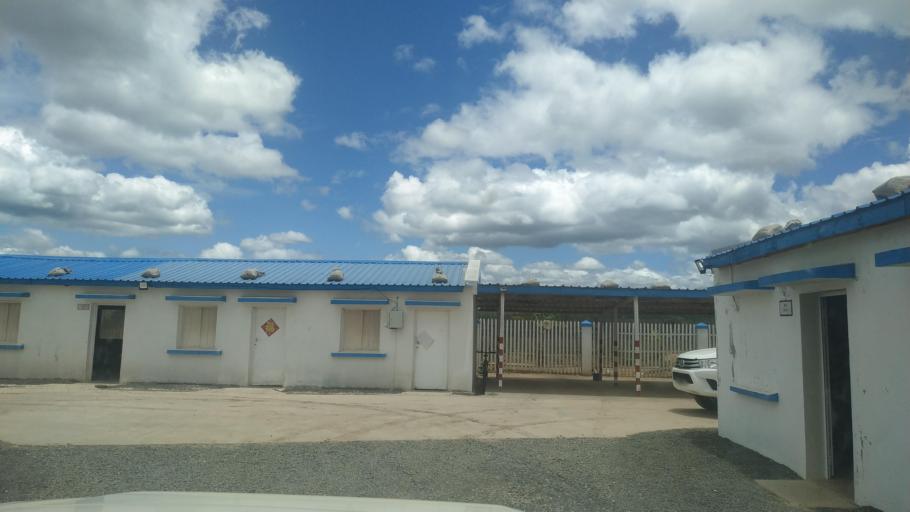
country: MG
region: Analamanga
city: Anjozorobe
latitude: -18.2748
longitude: 48.2626
